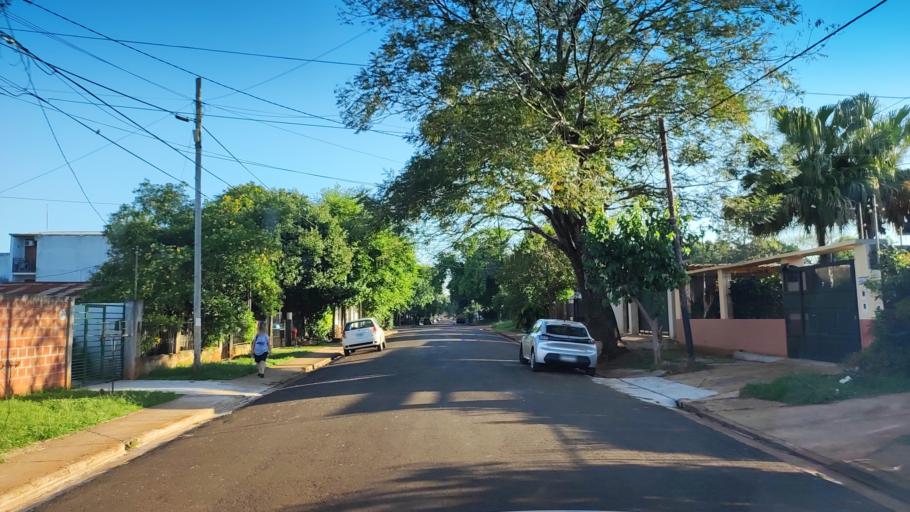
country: AR
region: Misiones
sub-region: Departamento de Capital
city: Posadas
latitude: -27.3821
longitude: -55.9357
